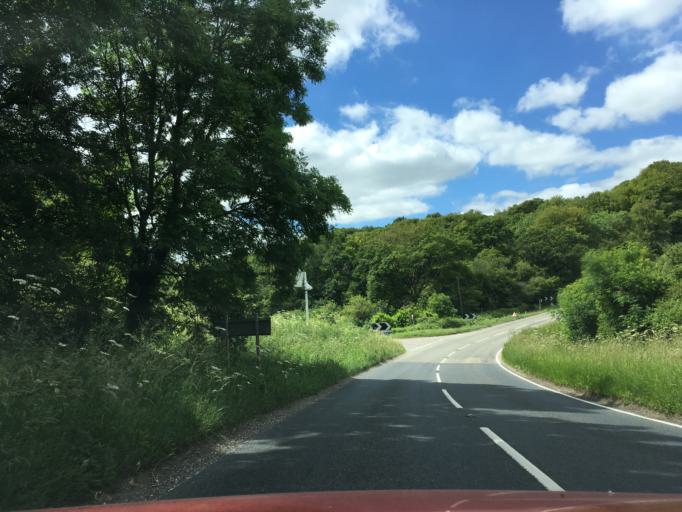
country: GB
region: England
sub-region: Hampshire
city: Highclere
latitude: 51.2935
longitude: -1.4182
